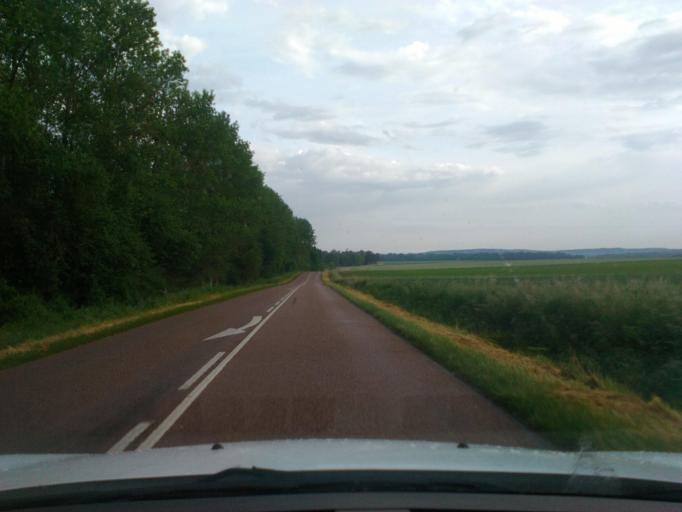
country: FR
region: Lorraine
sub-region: Departement des Vosges
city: Rambervillers
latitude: 48.4053
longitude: 6.5880
